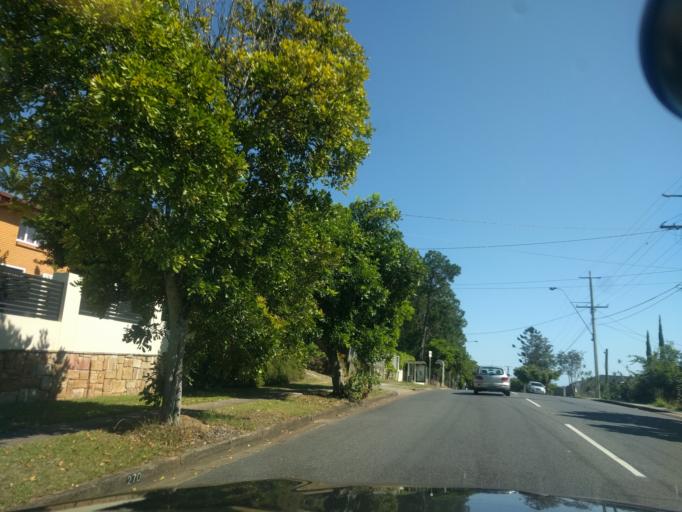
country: AU
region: Queensland
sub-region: Brisbane
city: Chermside West
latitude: -27.3717
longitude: 153.0149
